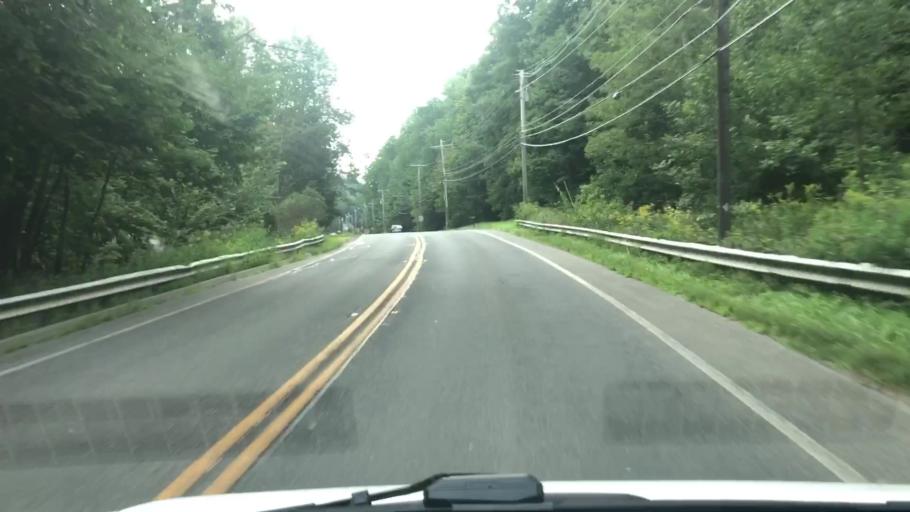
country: US
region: Massachusetts
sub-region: Berkshire County
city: Williamstown
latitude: 42.7083
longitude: -73.2218
